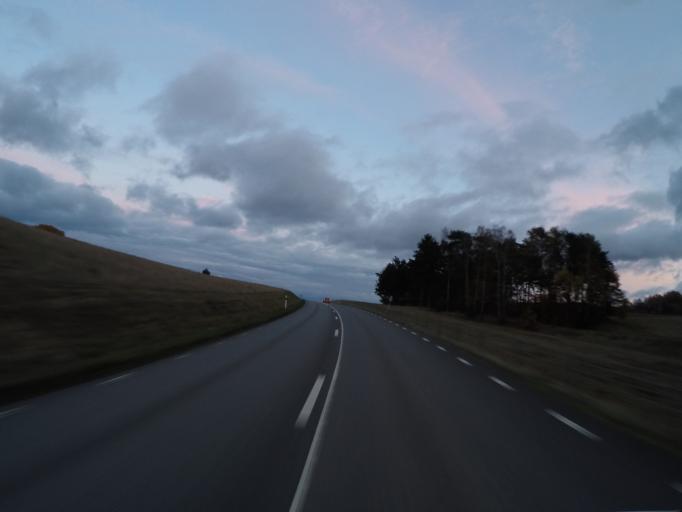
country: SE
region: Skane
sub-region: Kristianstads Kommun
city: Degeberga
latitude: 55.8244
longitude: 14.1067
